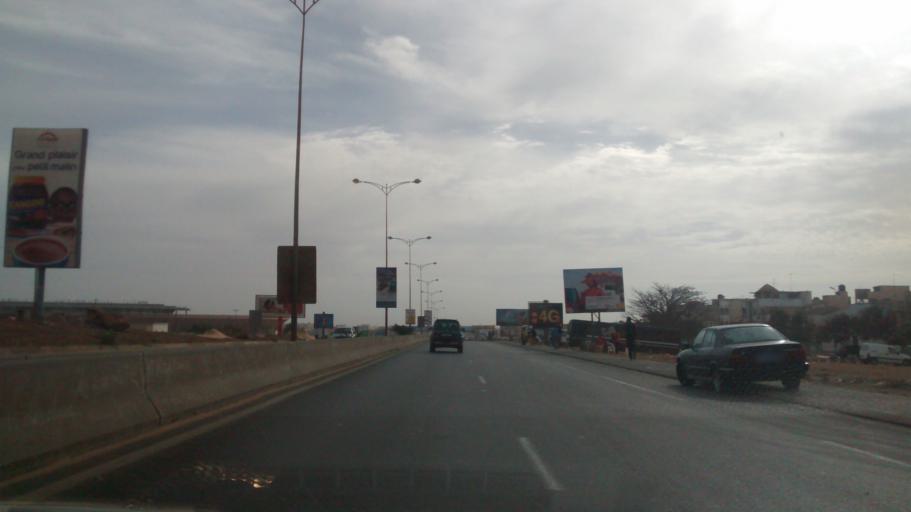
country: SN
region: Dakar
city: Grand Dakar
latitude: 14.7454
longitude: -17.4576
